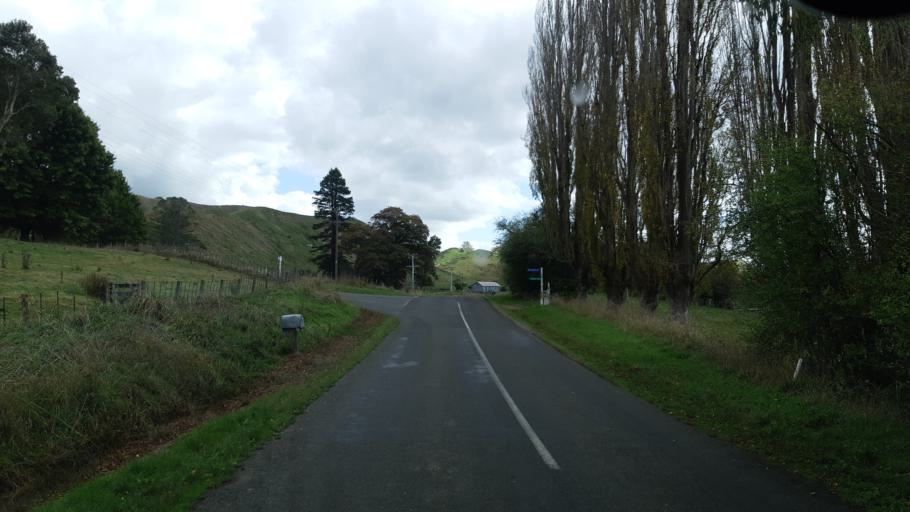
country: NZ
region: Manawatu-Wanganui
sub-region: Rangitikei District
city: Bulls
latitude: -39.9022
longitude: 175.5251
